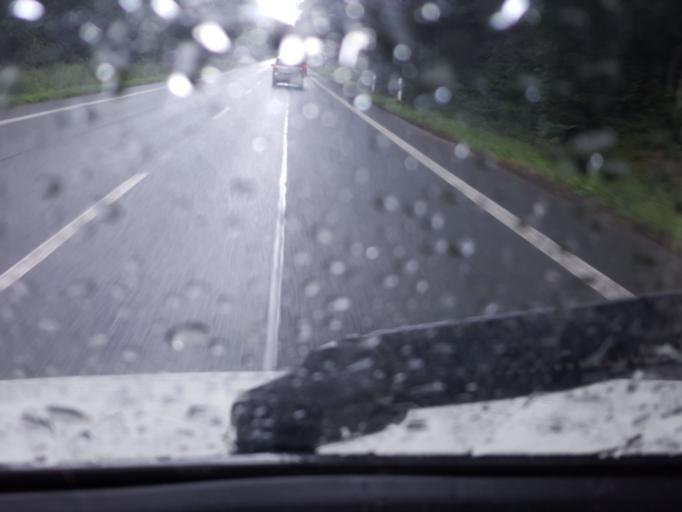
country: DE
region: North Rhine-Westphalia
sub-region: Regierungsbezirk Detmold
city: Petershagen
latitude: 52.3491
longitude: 8.9480
